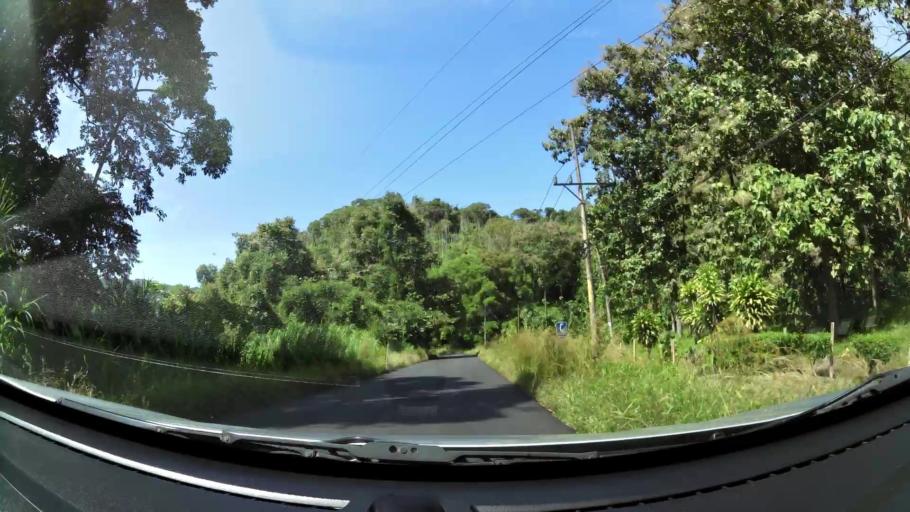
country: CR
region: San Jose
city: San Isidro
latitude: 9.2823
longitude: -83.8488
